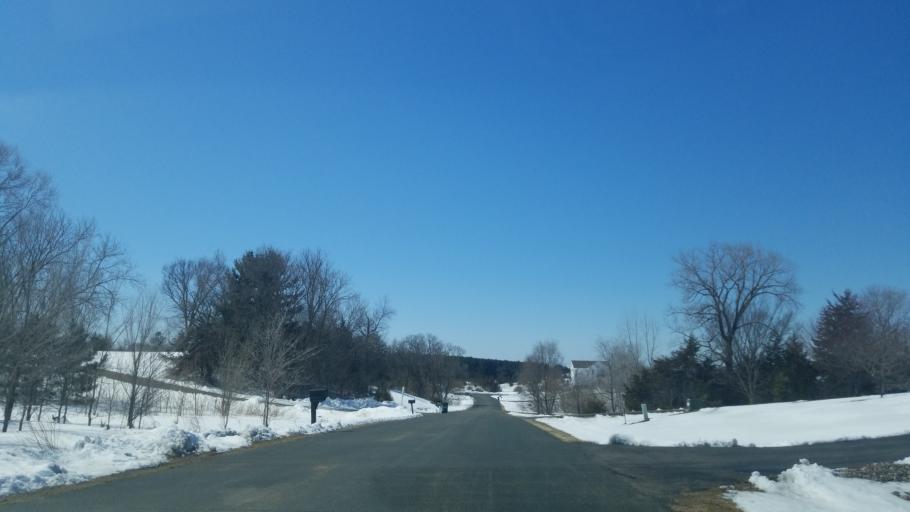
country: US
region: Wisconsin
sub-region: Saint Croix County
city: North Hudson
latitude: 44.9940
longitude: -92.6565
